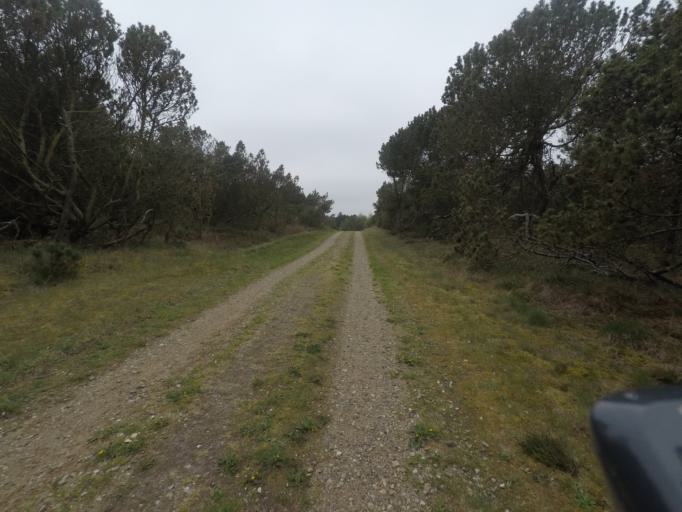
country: DE
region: Schleswig-Holstein
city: List
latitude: 55.1236
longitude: 8.5235
